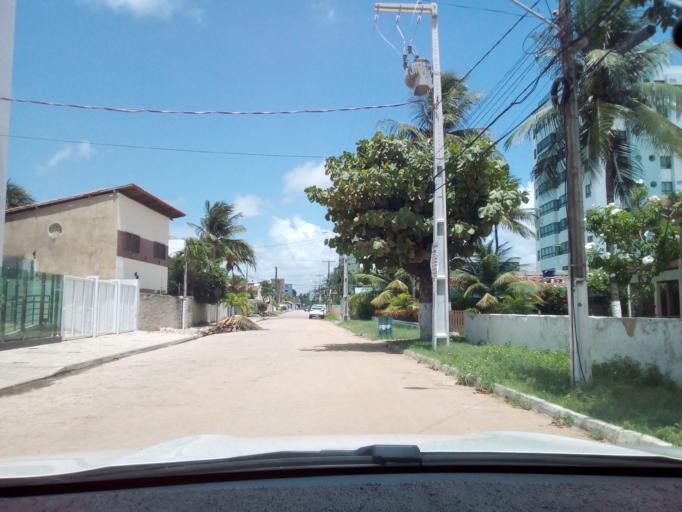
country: BR
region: Paraiba
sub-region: Cabedelo
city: Cabedelo
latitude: -7.0131
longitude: -34.8287
